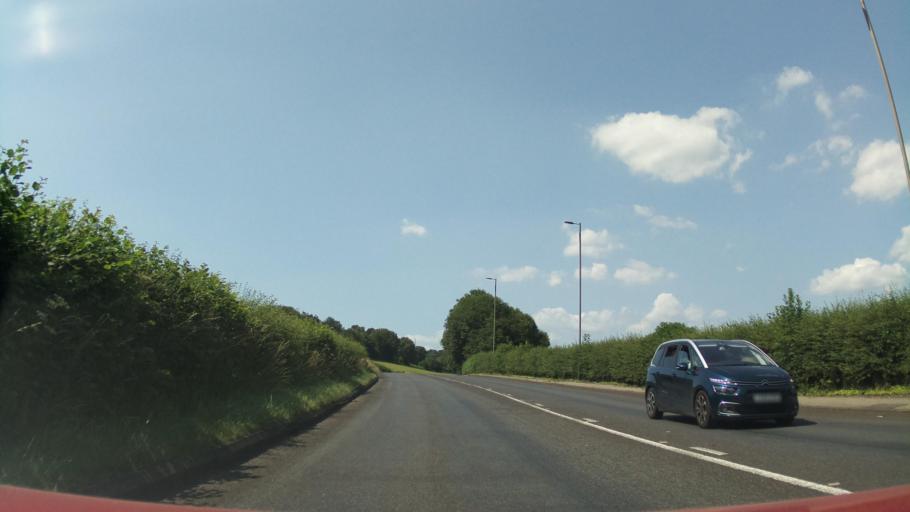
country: GB
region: Wales
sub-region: Caerphilly County Borough
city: Hengoed
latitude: 51.6546
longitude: -3.2252
